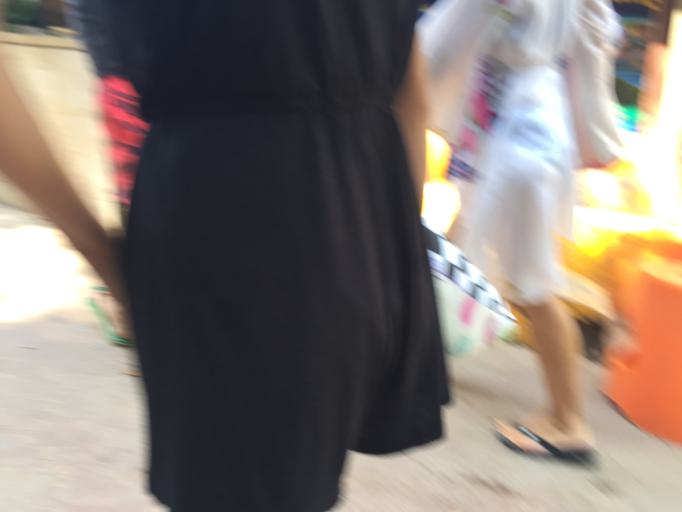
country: TH
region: Phangnga
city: Ban Ao Nang
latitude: 8.0116
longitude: 98.8421
